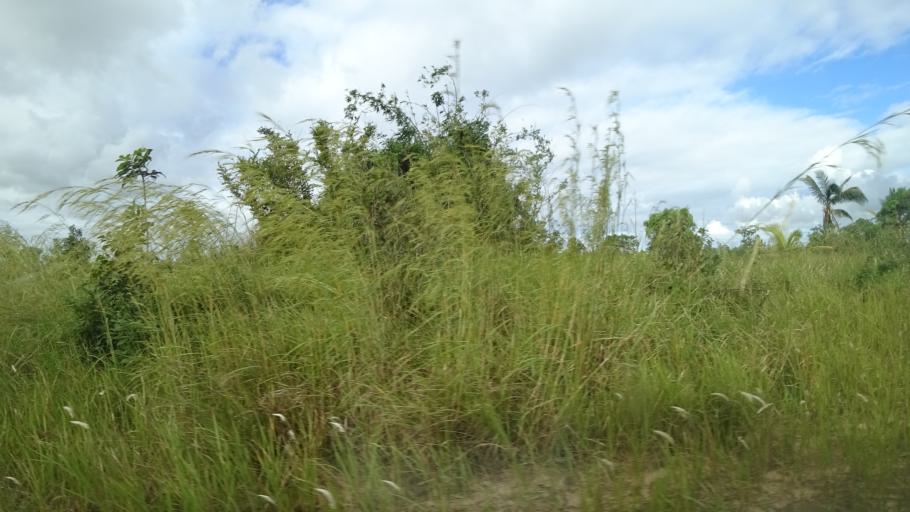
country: MZ
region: Sofala
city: Beira
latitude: -19.6345
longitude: 35.0596
